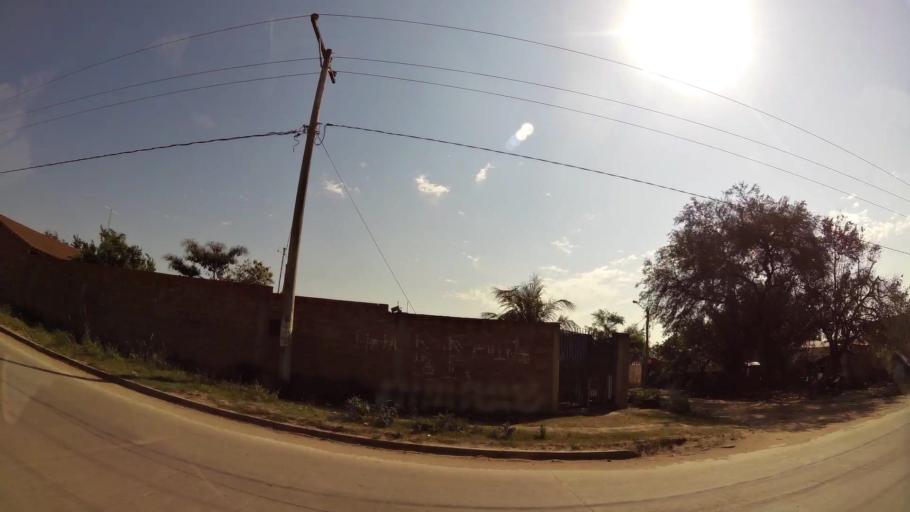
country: BO
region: Santa Cruz
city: Cotoca
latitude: -17.7988
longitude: -63.1090
